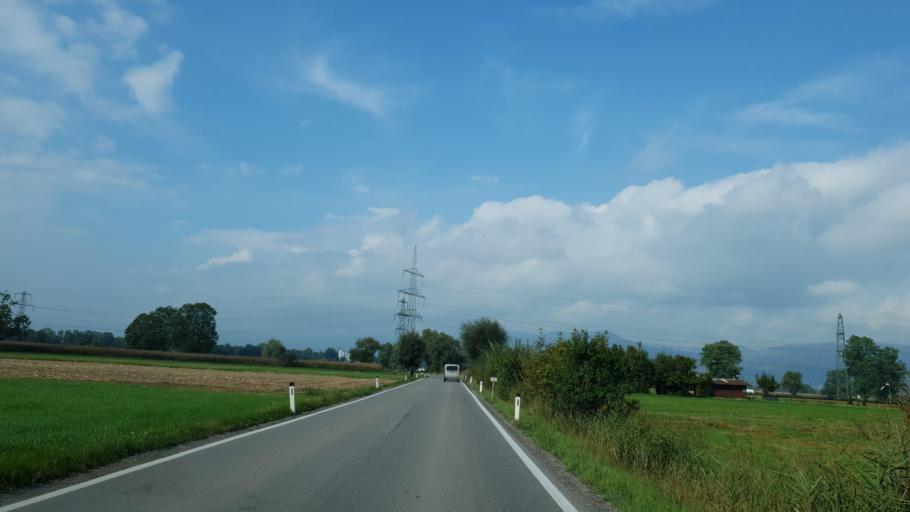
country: AT
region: Vorarlberg
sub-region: Politischer Bezirk Dornbirn
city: Hohenems
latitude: 47.3998
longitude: 9.6910
